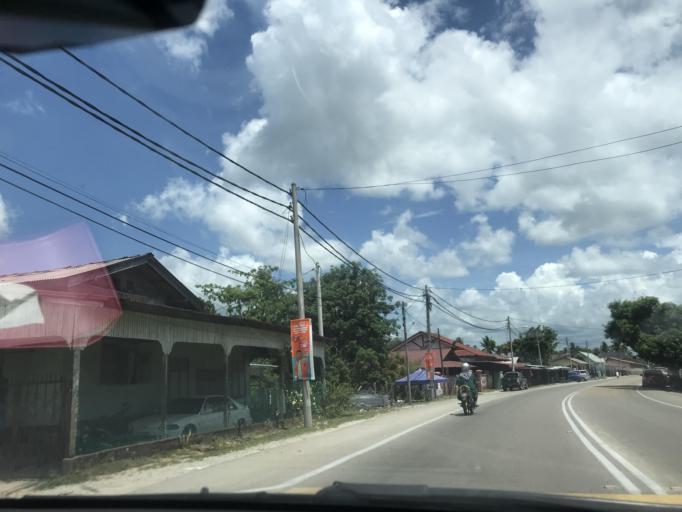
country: TH
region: Narathiwat
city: Tak Bai
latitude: 6.2227
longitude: 102.1076
